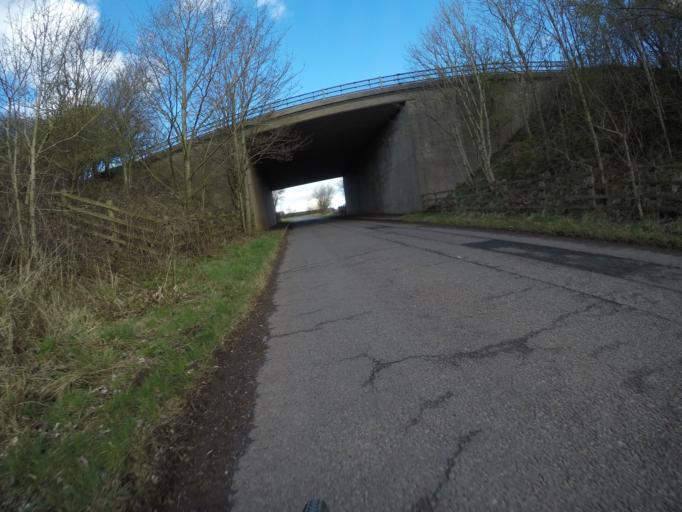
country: GB
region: Scotland
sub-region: East Ayrshire
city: Crosshouse
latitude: 55.6044
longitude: -4.5743
